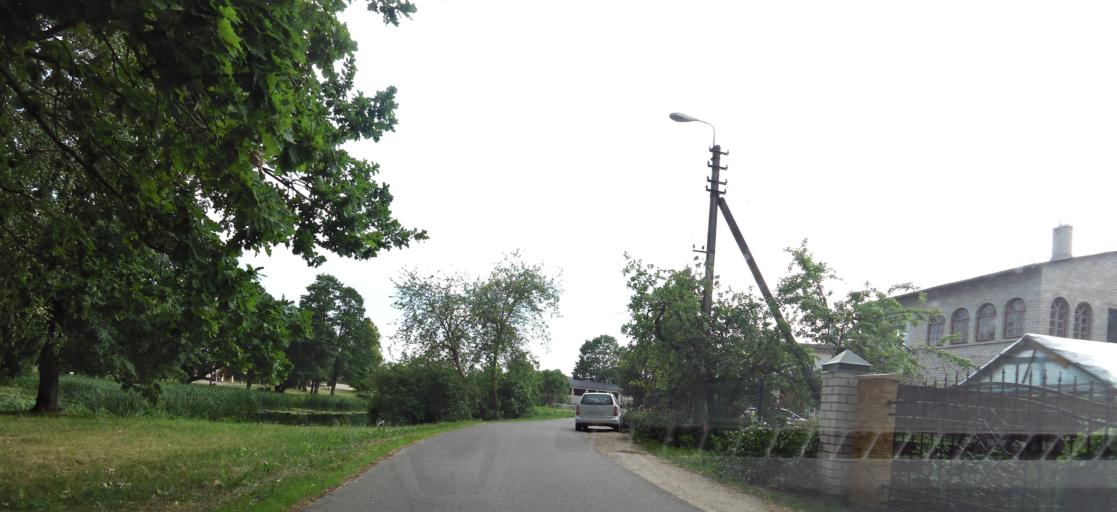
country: LT
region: Panevezys
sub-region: Birzai
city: Birzai
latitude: 56.2038
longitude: 24.7646
